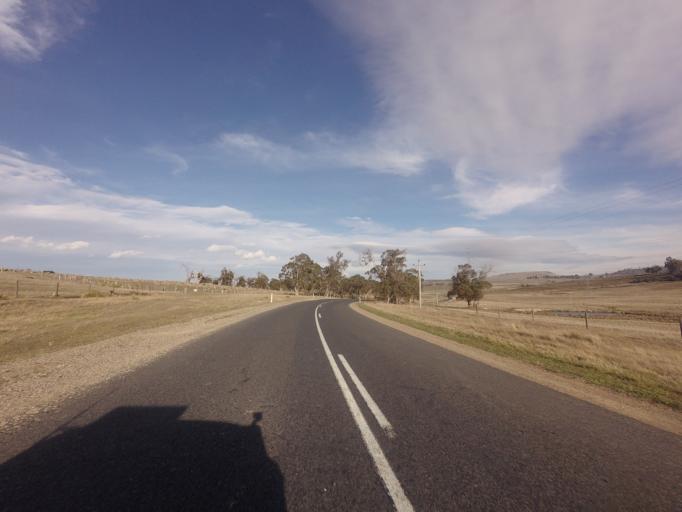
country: AU
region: Tasmania
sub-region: Derwent Valley
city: New Norfolk
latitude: -42.2581
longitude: 146.9373
